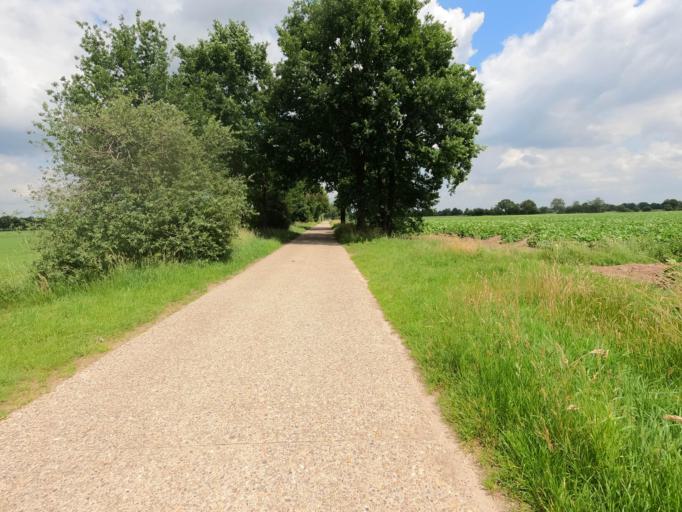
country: BE
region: Flanders
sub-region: Provincie Antwerpen
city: Kalmthout
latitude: 51.4149
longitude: 4.5117
